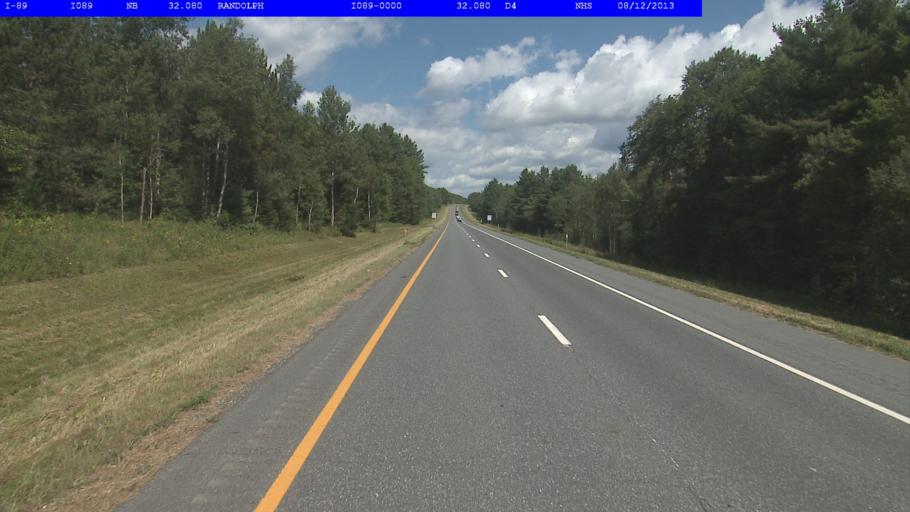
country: US
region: Vermont
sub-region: Orange County
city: Randolph
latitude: 43.9614
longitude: -72.6234
